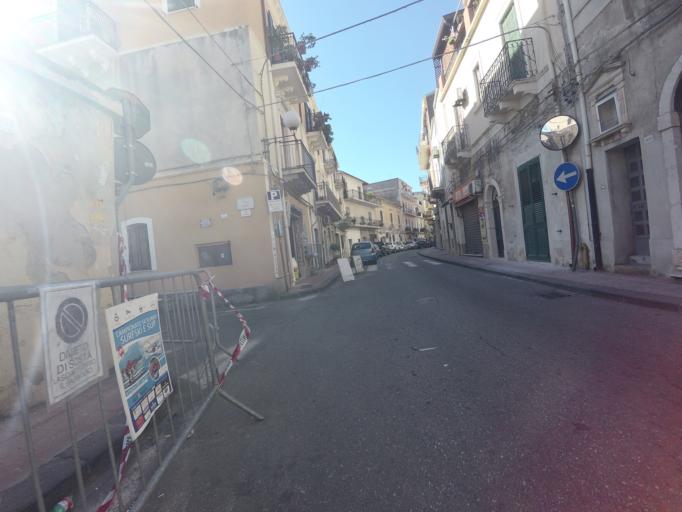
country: IT
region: Sicily
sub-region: Messina
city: Giardini-Naxos
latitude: 37.8386
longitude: 15.2759
